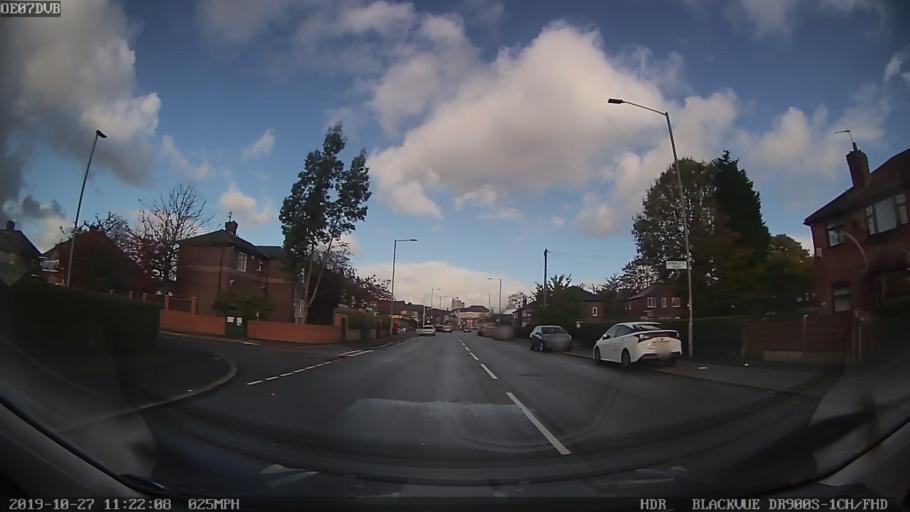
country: GB
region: England
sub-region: Manchester
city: Failsworth
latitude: 53.5202
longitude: -2.1819
